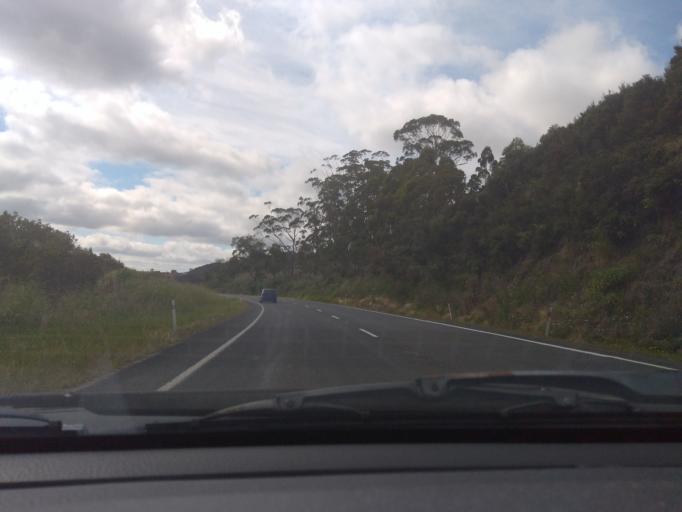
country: NZ
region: Northland
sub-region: Far North District
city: Taipa
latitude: -35.0080
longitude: 173.5398
